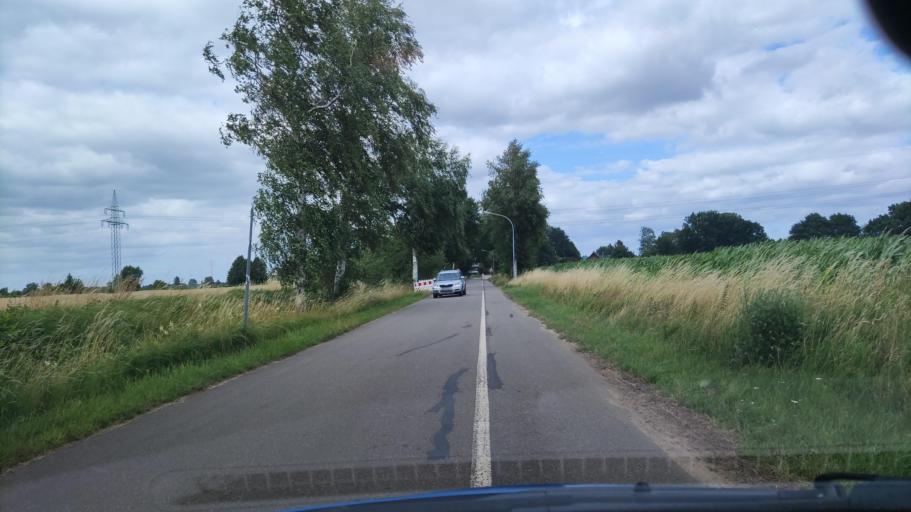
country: DE
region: Lower Saxony
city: Stelle
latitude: 53.4185
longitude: 10.0726
